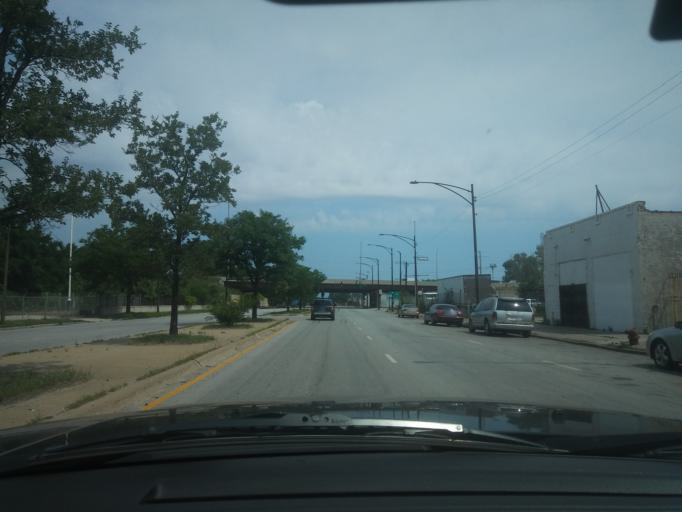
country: US
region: Illinois
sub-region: Cook County
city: Chicago
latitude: 41.7736
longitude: -87.6251
